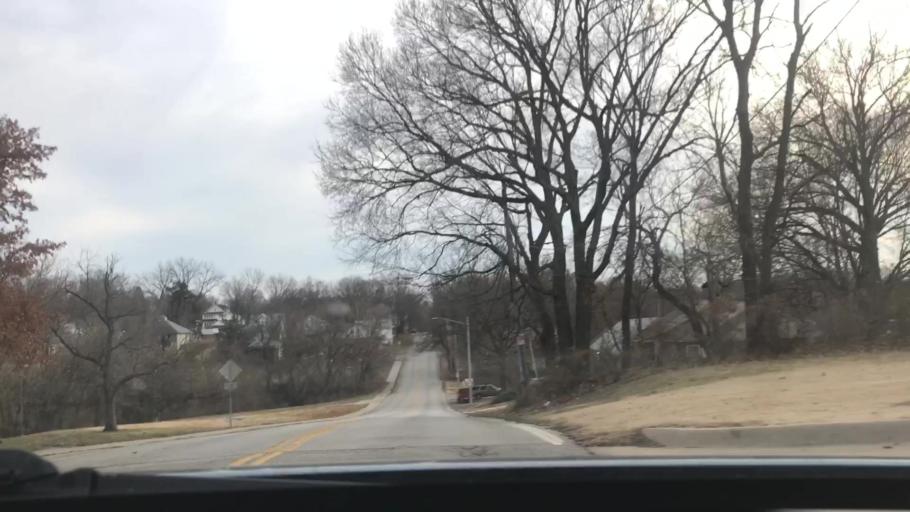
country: US
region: Missouri
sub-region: Jackson County
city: Sugar Creek
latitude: 39.0928
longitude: -94.4365
